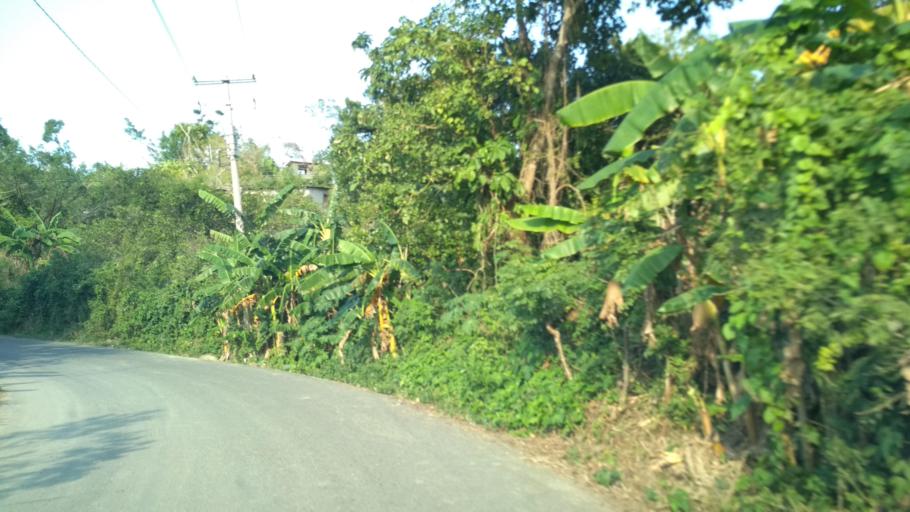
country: MX
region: Veracruz
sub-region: Poza Rica de Hidalgo
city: Arroyo del Maiz Uno
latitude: 20.4887
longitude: -97.3835
